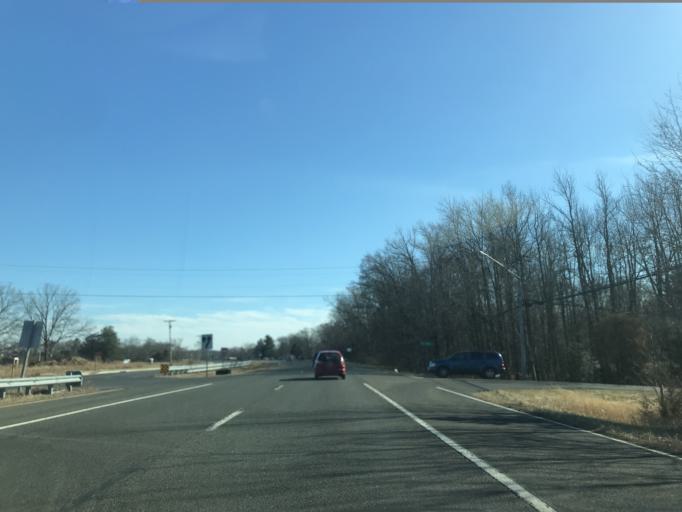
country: US
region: Maryland
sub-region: Charles County
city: Waldorf
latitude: 38.6433
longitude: -76.9332
